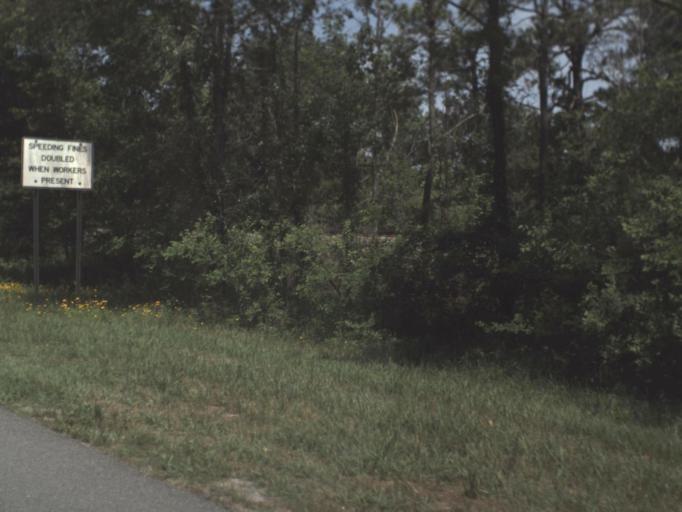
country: US
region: Florida
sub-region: Suwannee County
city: Live Oak
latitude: 30.3464
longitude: -83.0966
